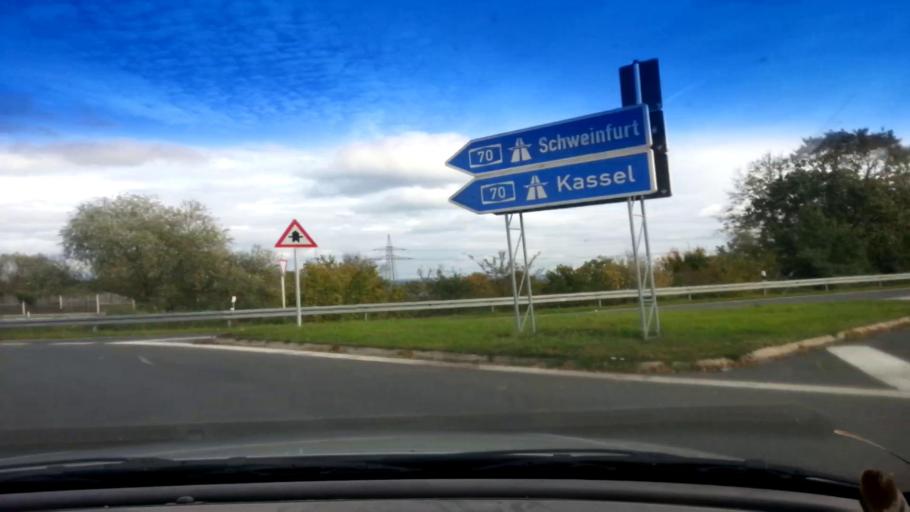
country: DE
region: Bavaria
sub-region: Upper Franconia
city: Hallstadt
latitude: 49.9221
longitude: 10.8751
